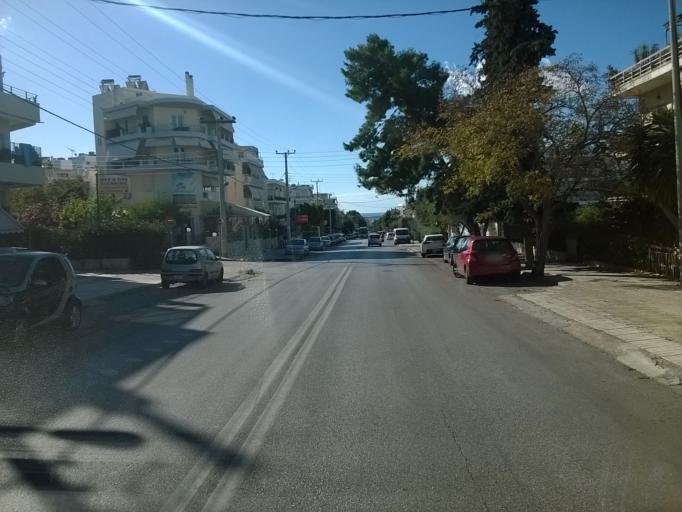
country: GR
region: Attica
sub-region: Nomarchia Athinas
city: Glyfada
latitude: 37.8826
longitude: 23.7592
